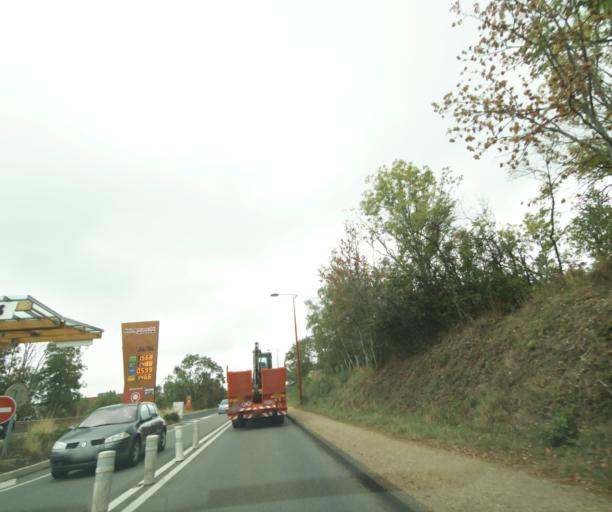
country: FR
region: Auvergne
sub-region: Departement du Puy-de-Dome
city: Ceyrat
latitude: 45.7493
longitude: 3.0626
